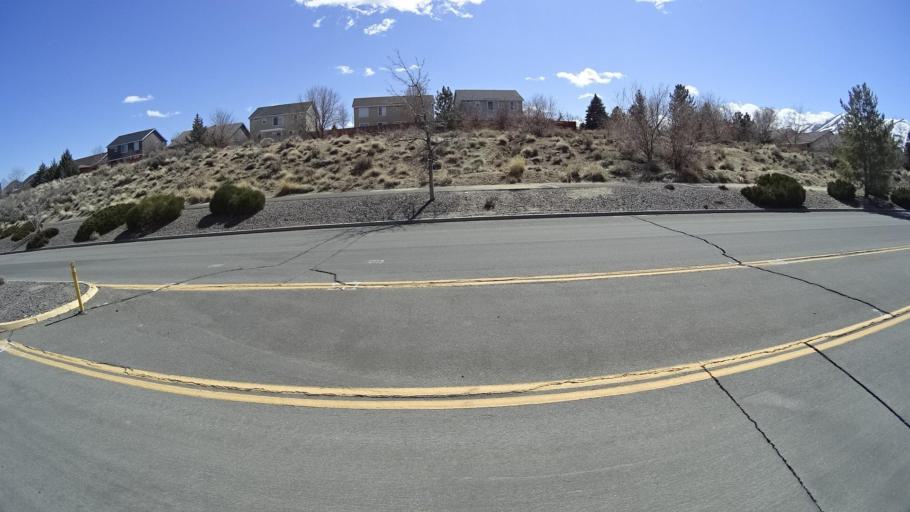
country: US
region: Nevada
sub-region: Washoe County
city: Lemmon Valley
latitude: 39.6417
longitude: -119.8736
